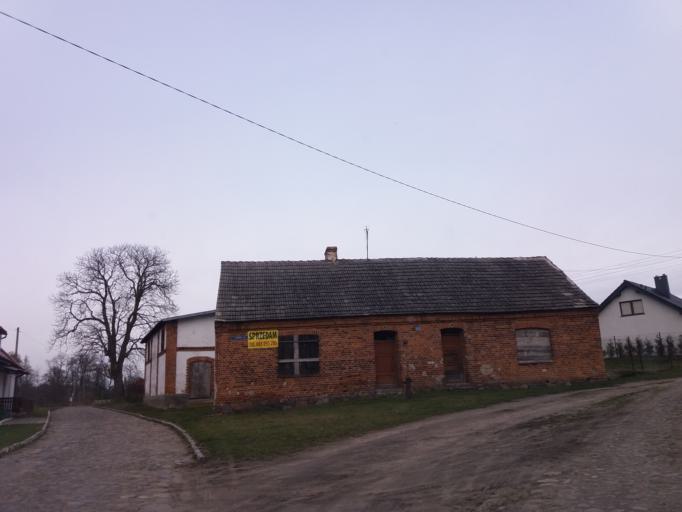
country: PL
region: West Pomeranian Voivodeship
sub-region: Powiat choszczenski
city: Krzecin
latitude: 53.1437
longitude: 15.5486
